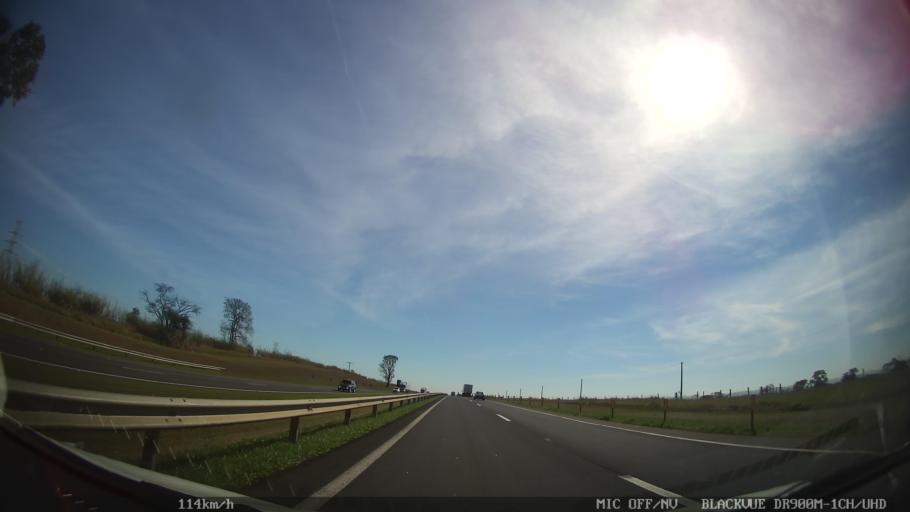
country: BR
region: Sao Paulo
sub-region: Pirassununga
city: Pirassununga
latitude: -21.9794
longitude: -47.4521
